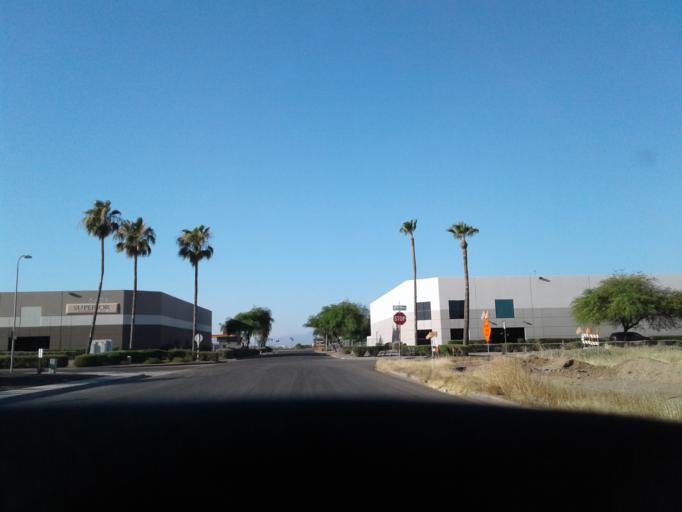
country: US
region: Arizona
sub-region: Maricopa County
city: Glendale
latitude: 33.4610
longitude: -112.1821
